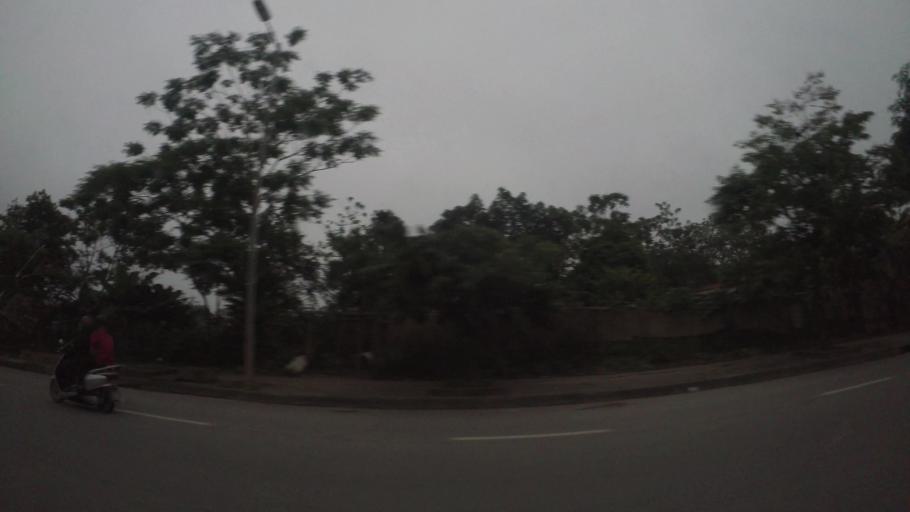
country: VN
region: Ha Noi
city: Van Dien
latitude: 20.9768
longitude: 105.8871
